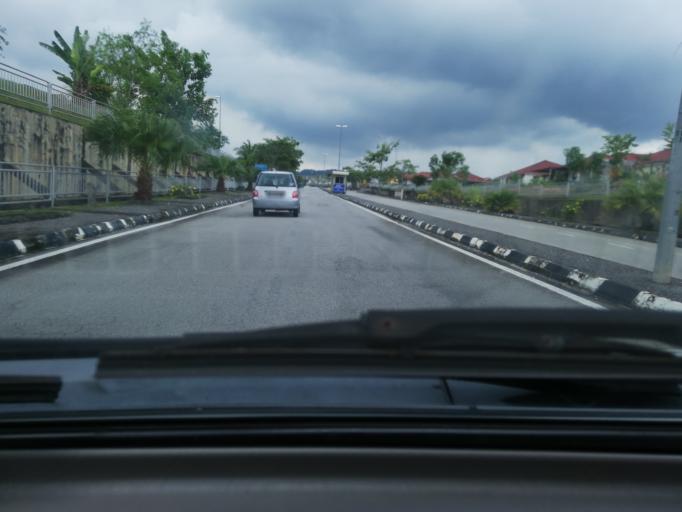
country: MY
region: Kedah
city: Kulim
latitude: 5.3880
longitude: 100.5799
